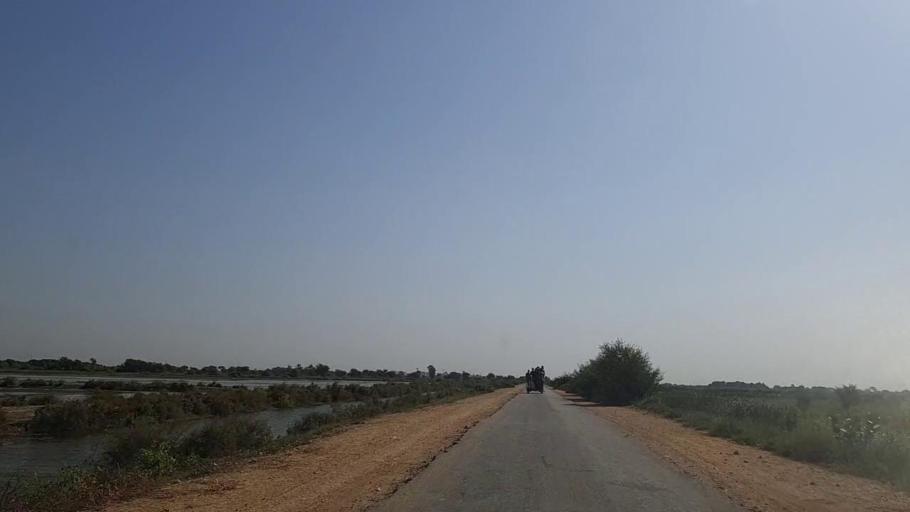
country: PK
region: Sindh
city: Mirpur Batoro
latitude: 24.6518
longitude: 68.2882
